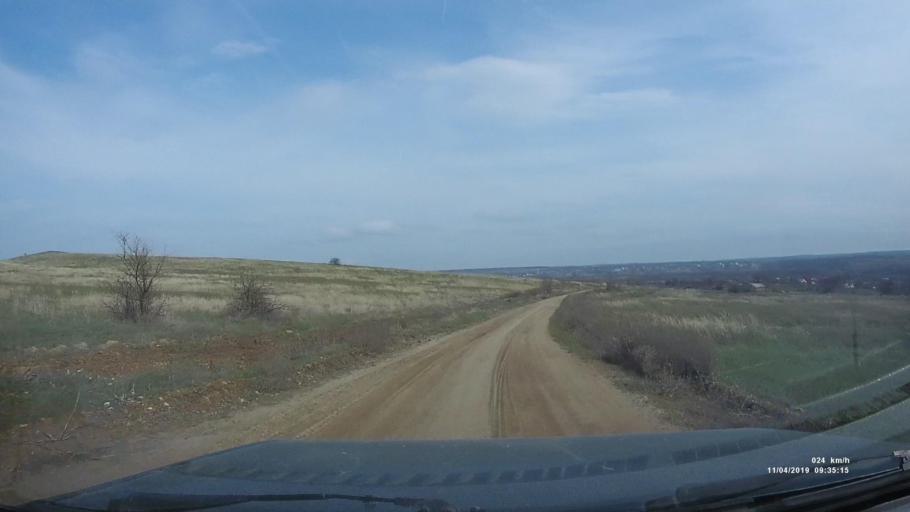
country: RU
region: Rostov
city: Staraya Stanitsa
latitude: 48.2719
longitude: 40.3718
